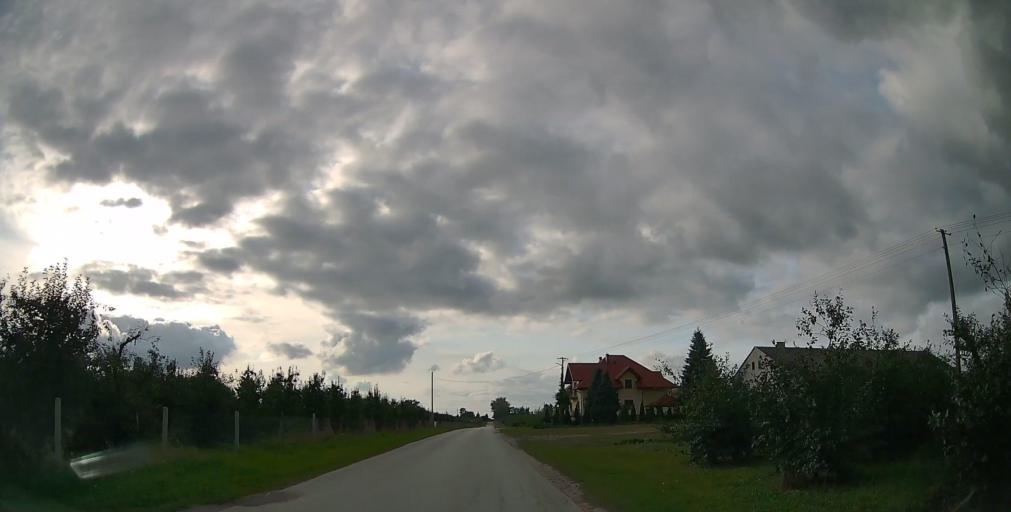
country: PL
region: Masovian Voivodeship
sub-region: Powiat grojecki
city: Jasieniec
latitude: 51.7562
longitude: 20.9195
